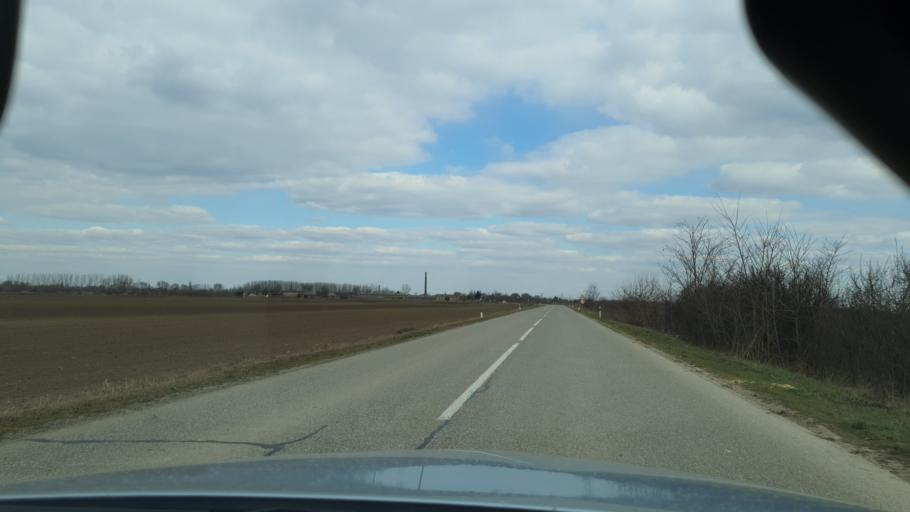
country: RS
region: Autonomna Pokrajina Vojvodina
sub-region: Zapadnobacki Okrug
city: Odzaci
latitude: 45.4427
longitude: 19.3179
